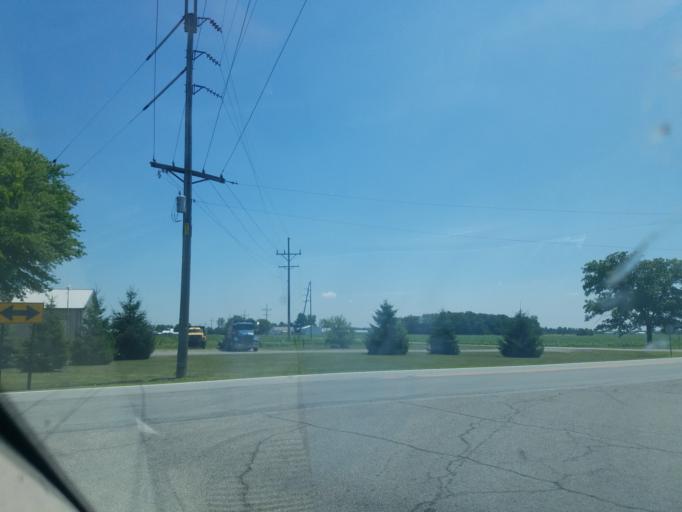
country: US
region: Ohio
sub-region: Allen County
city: Delphos
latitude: 40.7796
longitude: -84.3348
